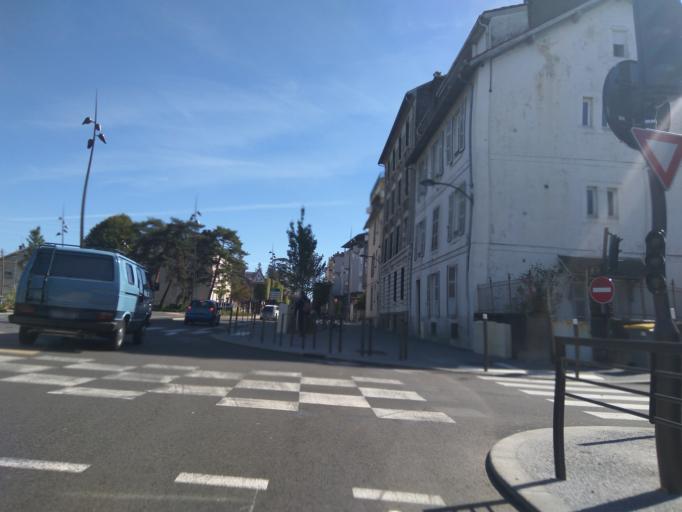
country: FR
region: Aquitaine
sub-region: Departement des Pyrenees-Atlantiques
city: Pau
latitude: 43.3043
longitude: -0.3677
